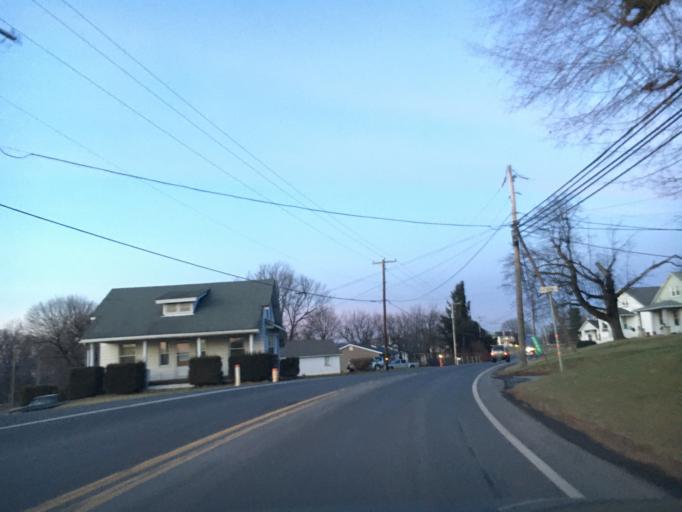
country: US
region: Pennsylvania
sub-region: Lehigh County
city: Schnecksville
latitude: 40.6845
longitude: -75.6133
